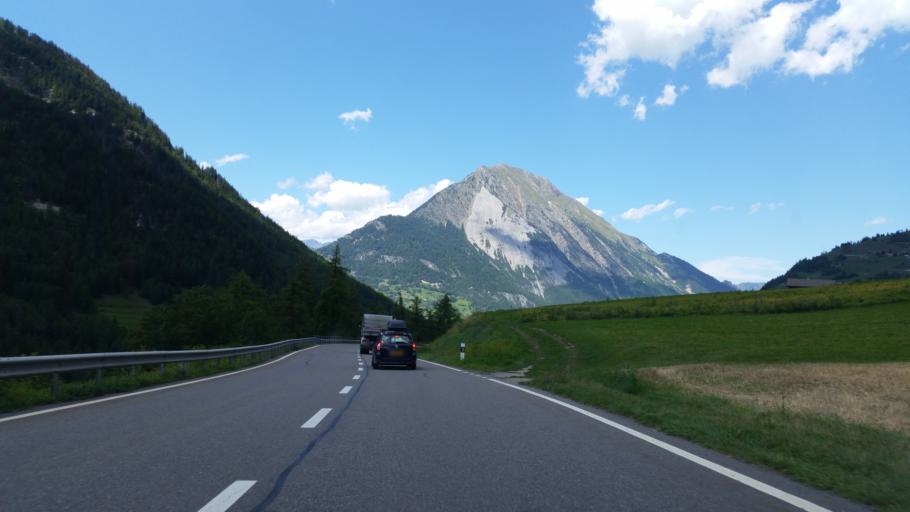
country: CH
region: Valais
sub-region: Entremont District
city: Orsieres
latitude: 46.0030
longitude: 7.1738
